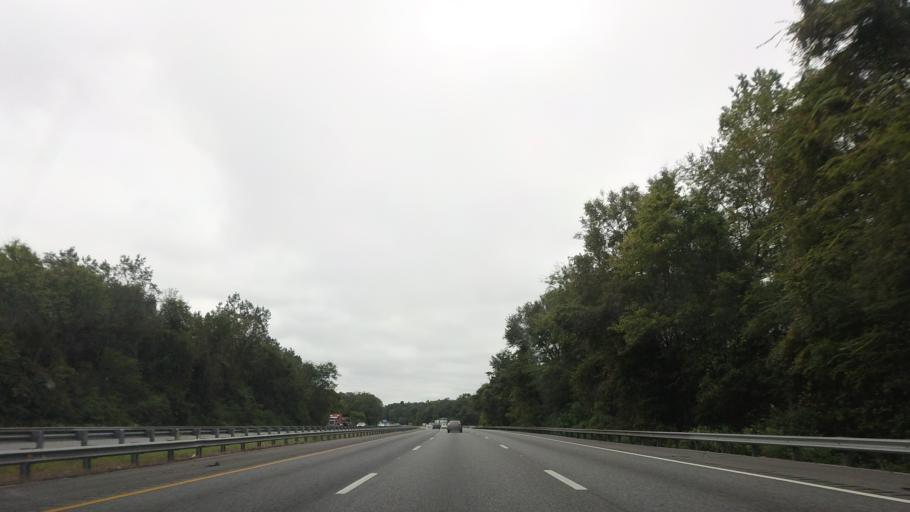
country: US
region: Florida
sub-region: Hamilton County
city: Jasper
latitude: 30.4982
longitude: -83.0402
